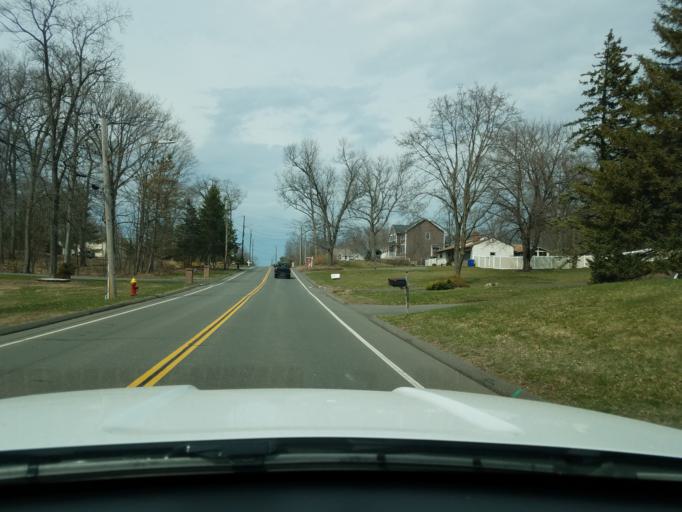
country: US
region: Connecticut
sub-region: Hartford County
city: Newington
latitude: 41.6540
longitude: -72.7155
